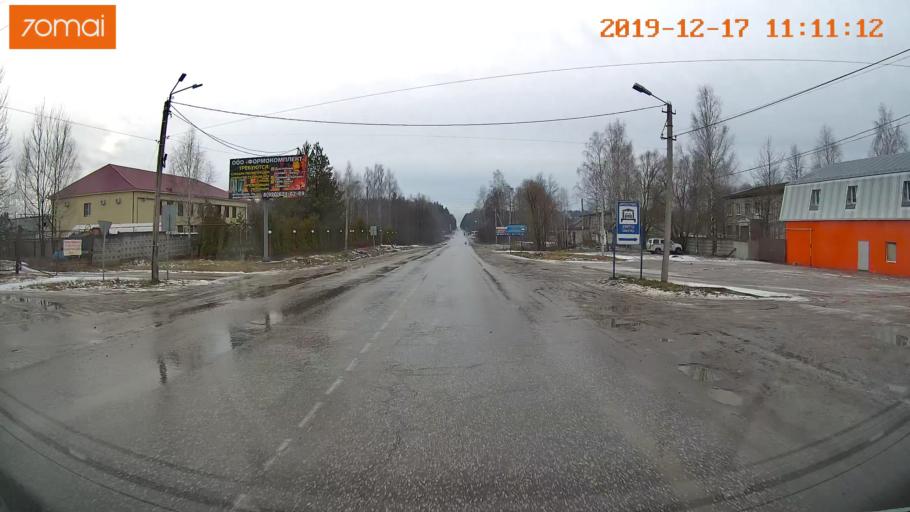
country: RU
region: Vladimir
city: Gus'-Khrustal'nyy
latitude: 55.5883
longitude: 40.6381
